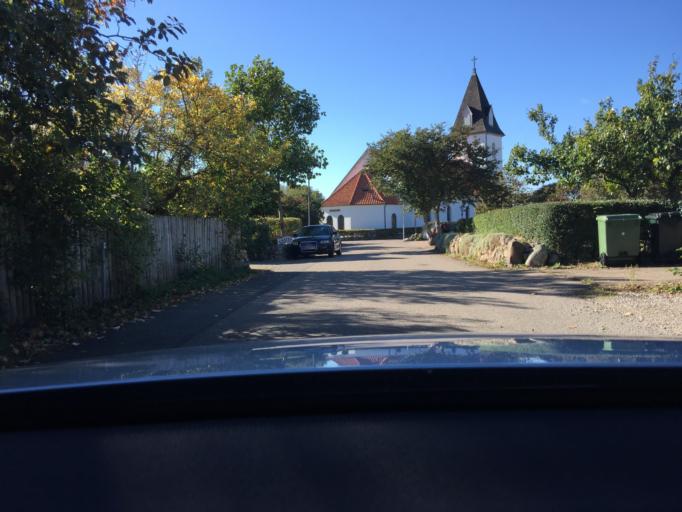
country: SE
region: Skane
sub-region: Hoganas Kommun
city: Hoganas
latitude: 56.1465
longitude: 12.5731
